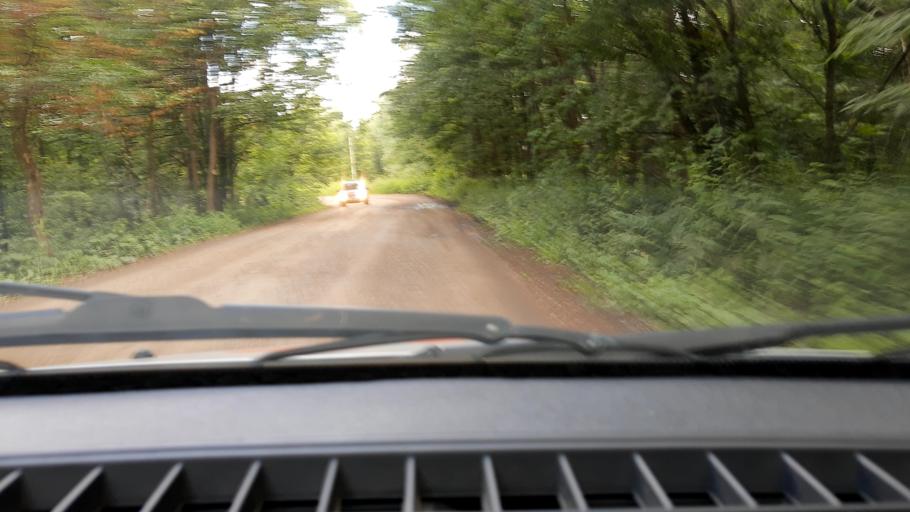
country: RU
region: Bashkortostan
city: Ufa
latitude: 54.6839
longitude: 56.0593
